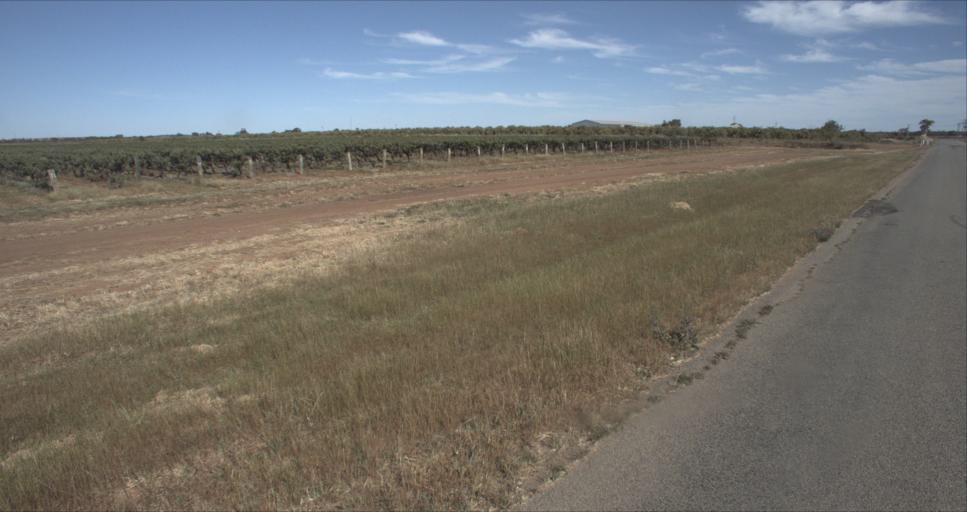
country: AU
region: New South Wales
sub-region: Leeton
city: Leeton
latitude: -34.5836
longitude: 146.3794
